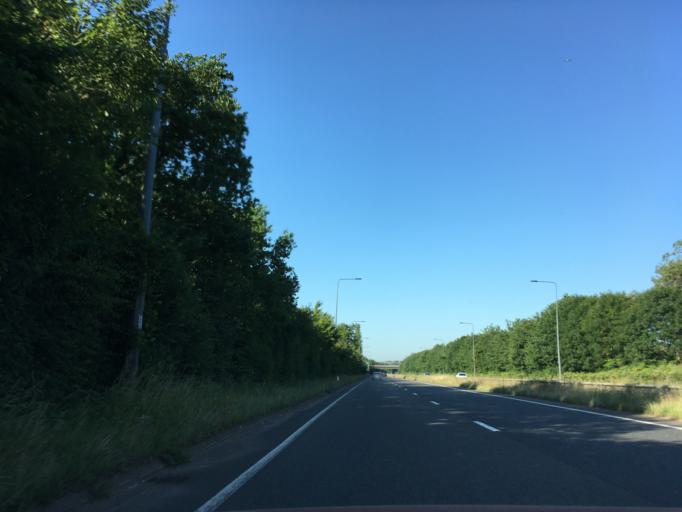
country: GB
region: England
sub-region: South Gloucestershire
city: Siston
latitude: 51.4767
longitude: -2.4763
